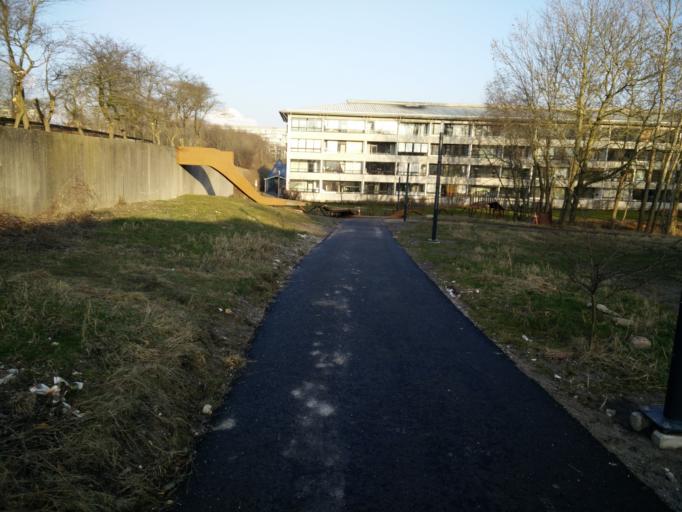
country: DK
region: Capital Region
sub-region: Herlev Kommune
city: Herlev
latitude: 55.7578
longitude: 12.4326
